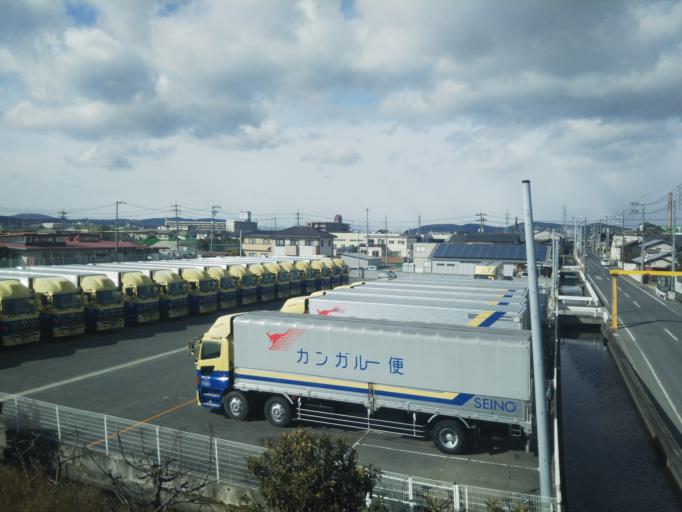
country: JP
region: Okayama
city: Okayama-shi
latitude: 34.6158
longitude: 133.8838
